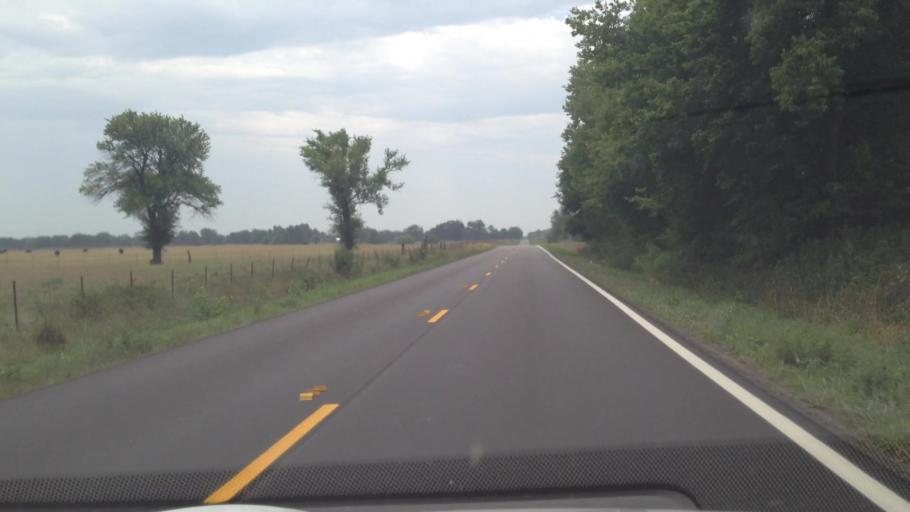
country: US
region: Kansas
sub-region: Crawford County
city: Girard
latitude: 37.5373
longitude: -94.9605
